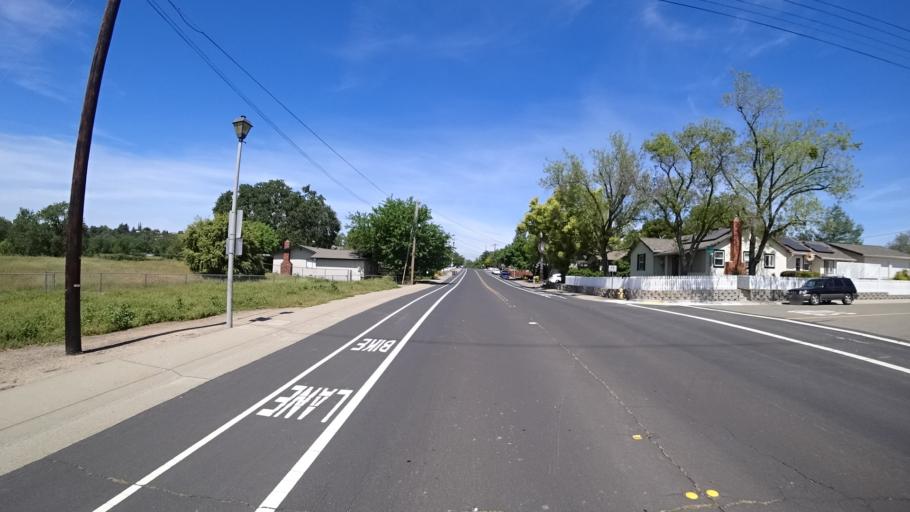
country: US
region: California
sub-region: Placer County
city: Rocklin
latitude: 38.7917
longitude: -121.2425
